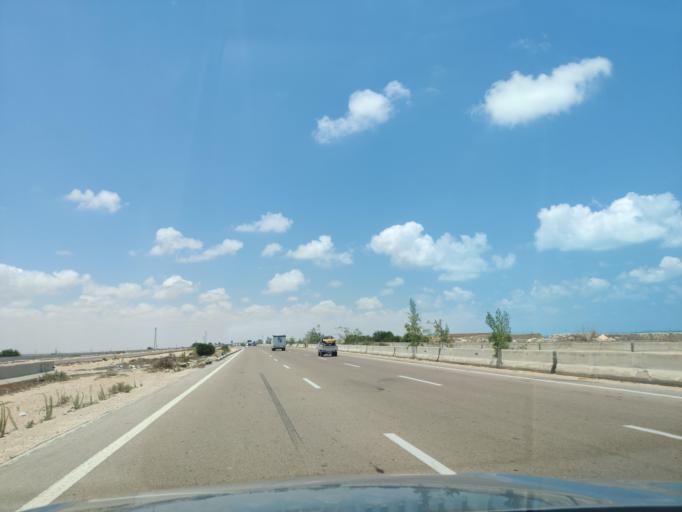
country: EG
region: Muhafazat Matruh
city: Al `Alamayn
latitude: 30.8125
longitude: 29.0813
